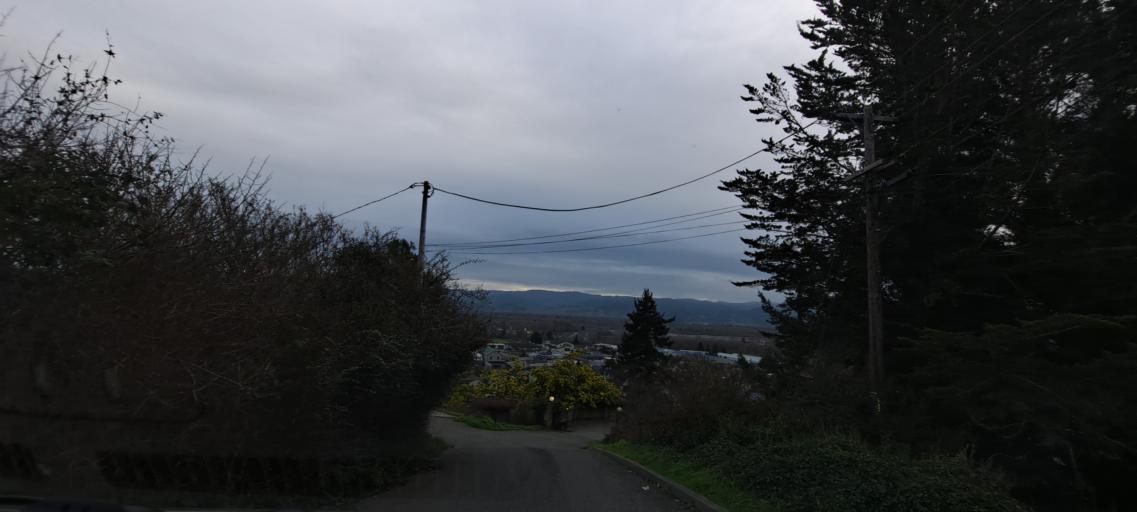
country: US
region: California
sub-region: Humboldt County
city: Fortuna
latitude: 40.6016
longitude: -124.1565
